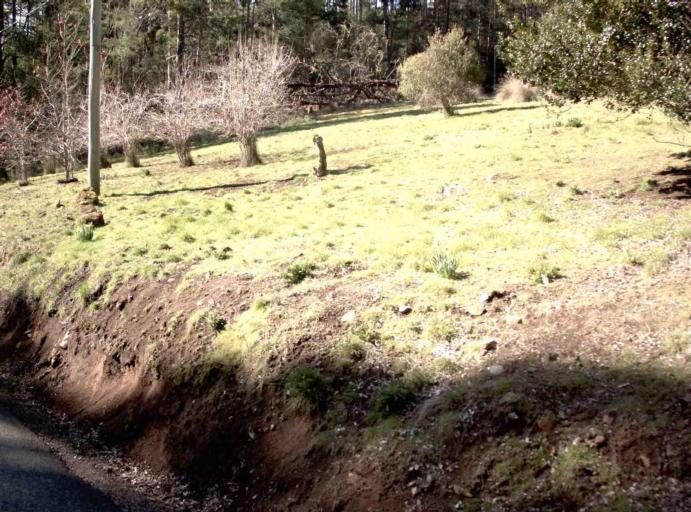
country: AU
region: Tasmania
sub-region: Launceston
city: Mayfield
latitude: -41.2984
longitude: 147.2000
